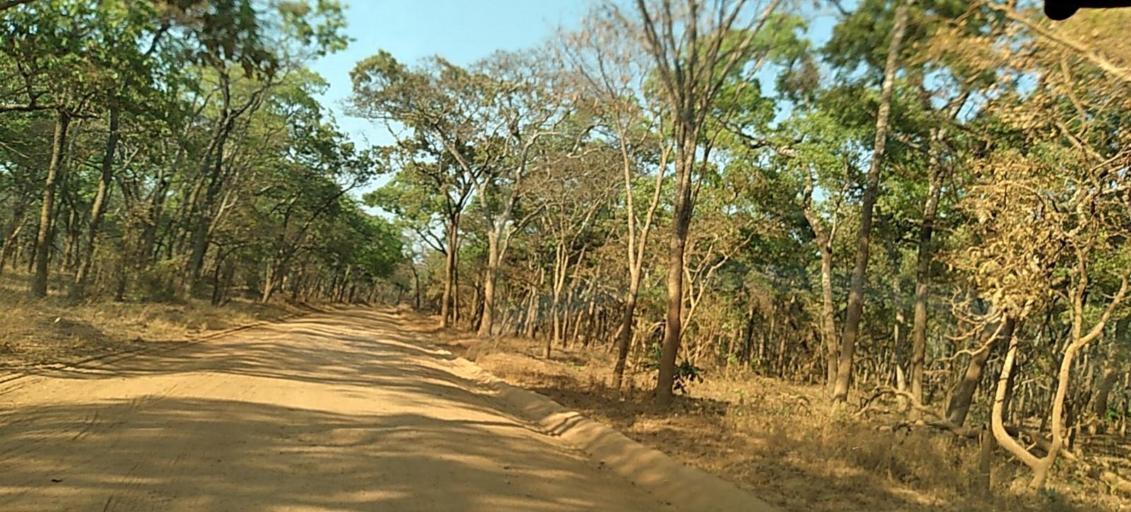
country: ZM
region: North-Western
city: Kasempa
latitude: -13.5851
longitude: 25.9868
